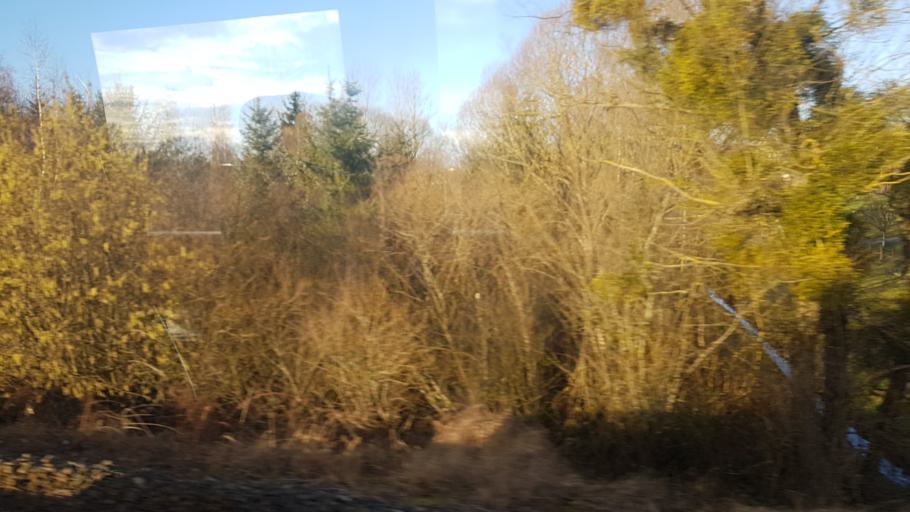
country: FR
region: Lorraine
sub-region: Departement des Vosges
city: Hadol
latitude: 48.1034
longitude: 6.4488
